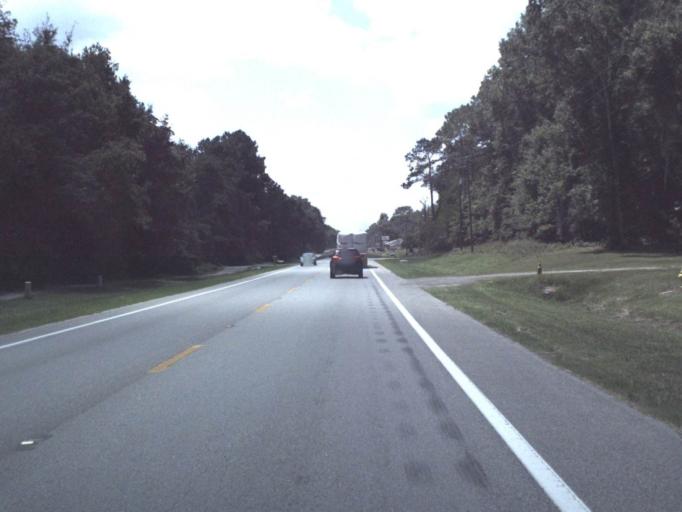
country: US
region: Florida
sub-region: Alachua County
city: High Springs
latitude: 29.9294
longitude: -82.7246
